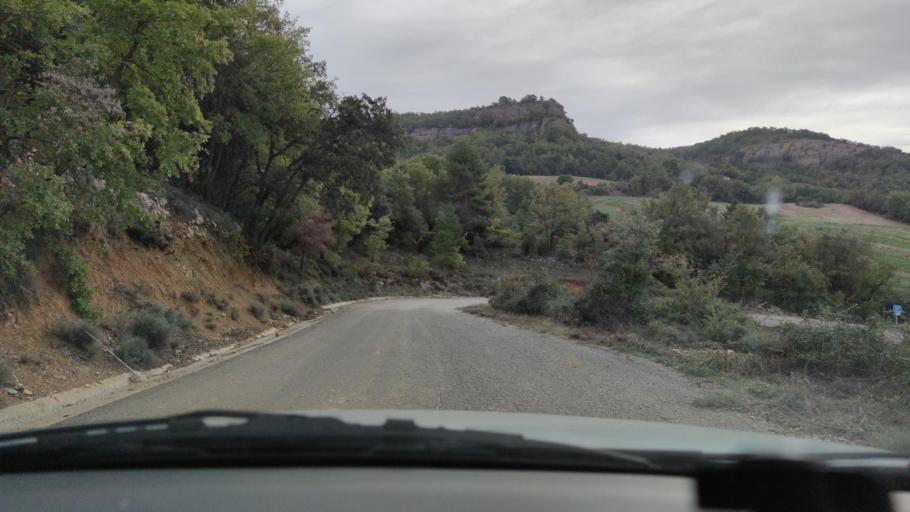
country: ES
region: Catalonia
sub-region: Provincia de Lleida
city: Llimiana
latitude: 42.0480
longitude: 0.9967
